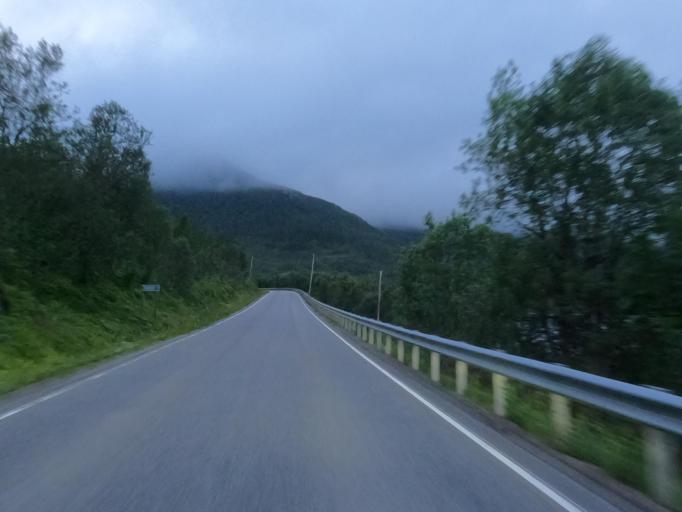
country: NO
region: Nordland
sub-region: Lodingen
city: Lodingen
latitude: 68.6116
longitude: 15.7754
